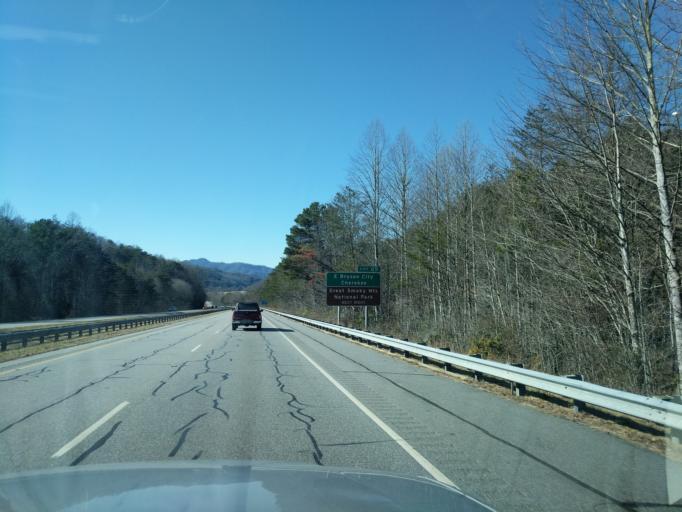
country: US
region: North Carolina
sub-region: Swain County
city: Bryson City
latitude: 35.4358
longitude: -83.3854
